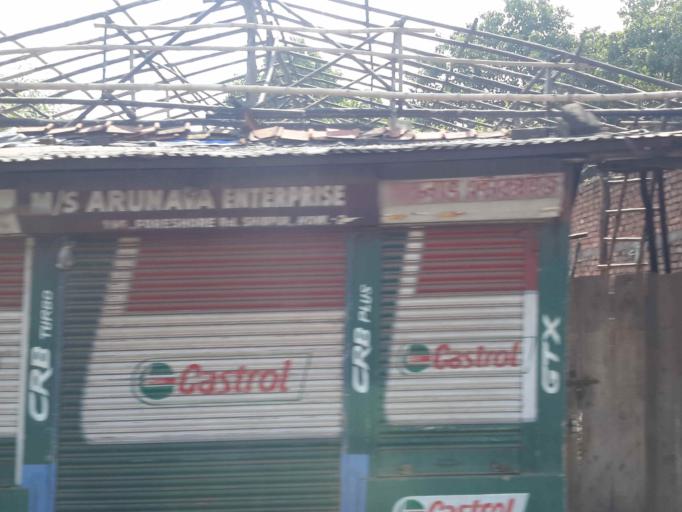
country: IN
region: West Bengal
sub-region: Haora
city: Haora
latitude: 22.5703
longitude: 88.3320
